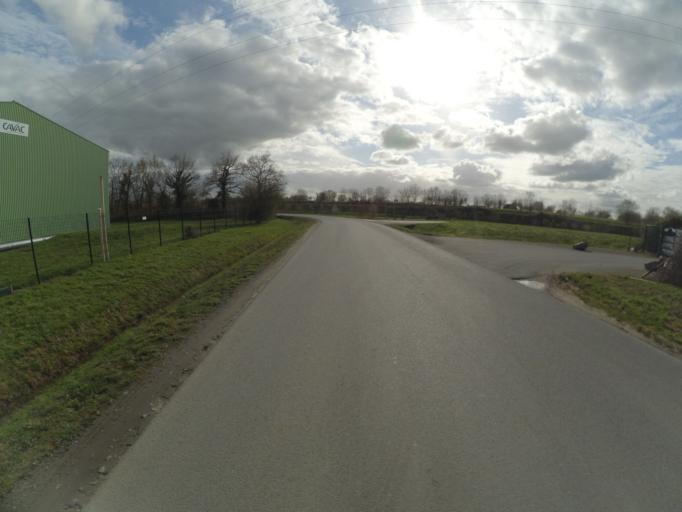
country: FR
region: Pays de la Loire
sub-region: Departement de la Vendee
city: Bouffere
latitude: 46.9666
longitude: -1.3273
